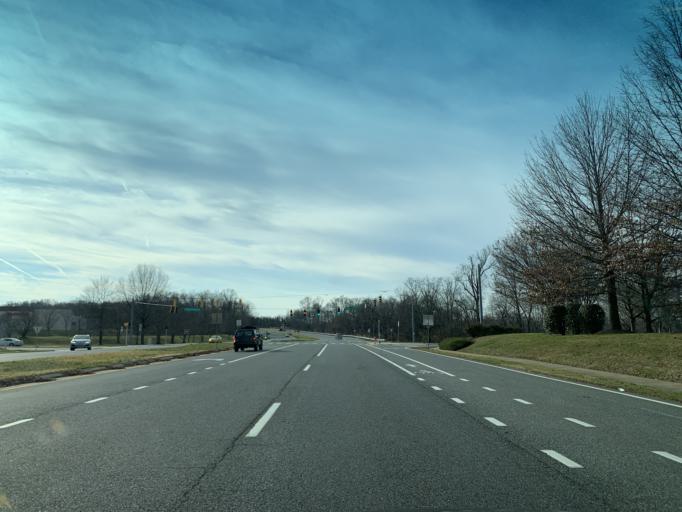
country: US
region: Delaware
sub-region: New Castle County
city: Pike Creek Valley
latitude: 39.6960
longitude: -75.6627
